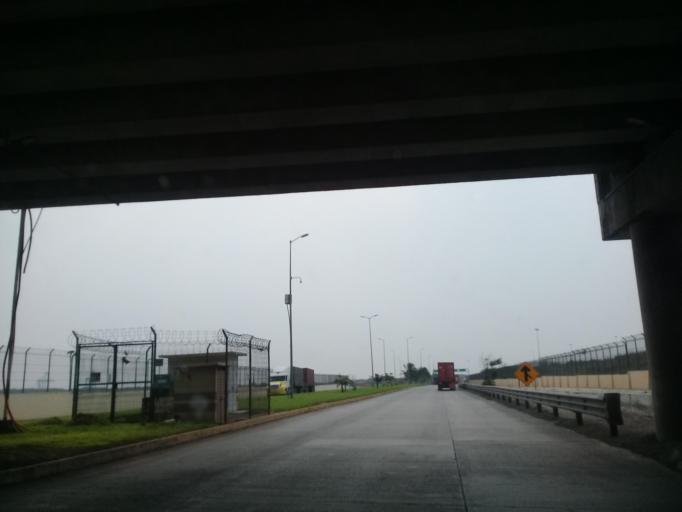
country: MX
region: Veracruz
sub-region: Veracruz
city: Rio Medio [Granja]
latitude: 19.2271
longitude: -96.1899
